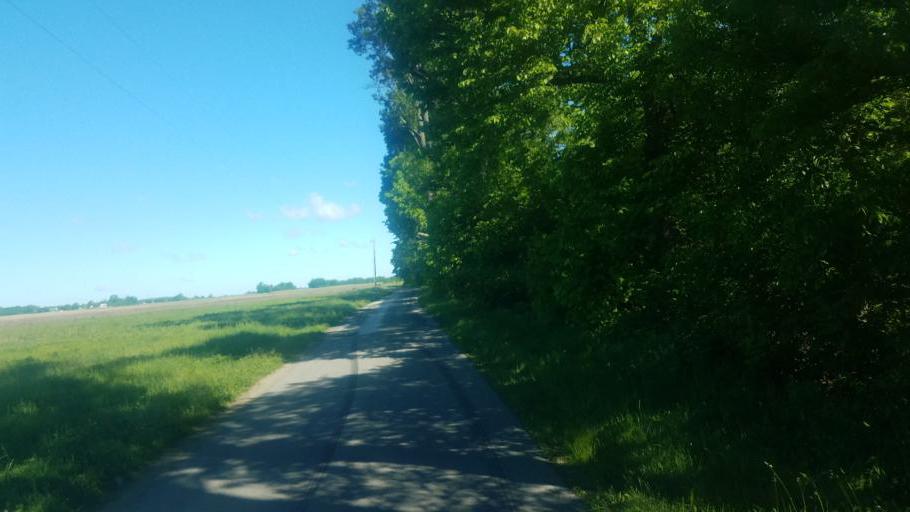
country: US
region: Ohio
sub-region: Marion County
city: Prospect
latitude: 40.5333
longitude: -83.2149
